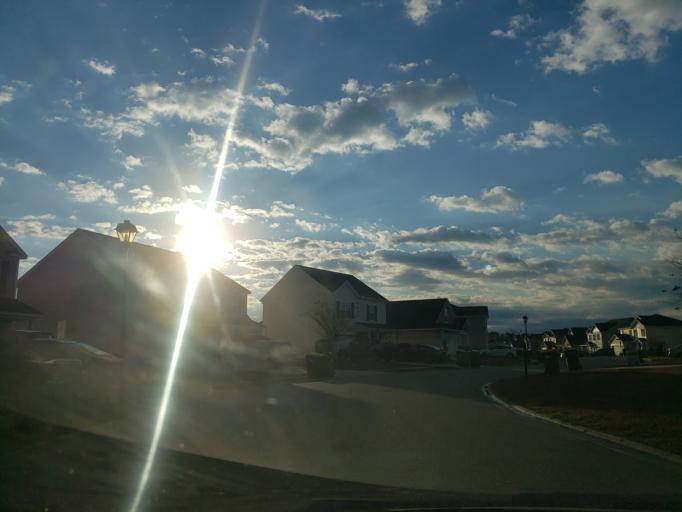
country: US
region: Georgia
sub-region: Chatham County
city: Bloomingdale
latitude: 32.1555
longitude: -81.2725
